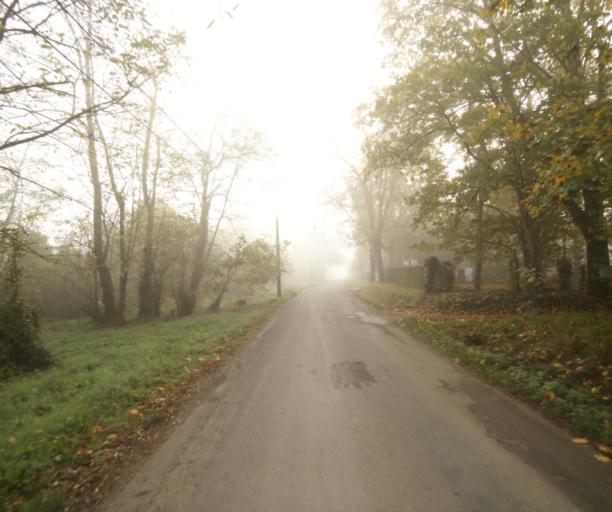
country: FR
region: Midi-Pyrenees
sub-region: Departement du Tarn-et-Garonne
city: Nohic
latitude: 43.9045
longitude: 1.4488
